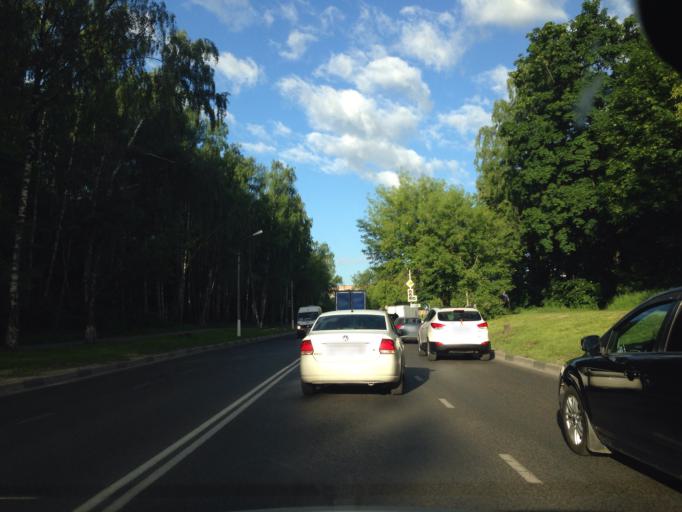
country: RU
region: Moskovskaya
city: Balashikha
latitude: 55.8064
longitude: 37.9428
